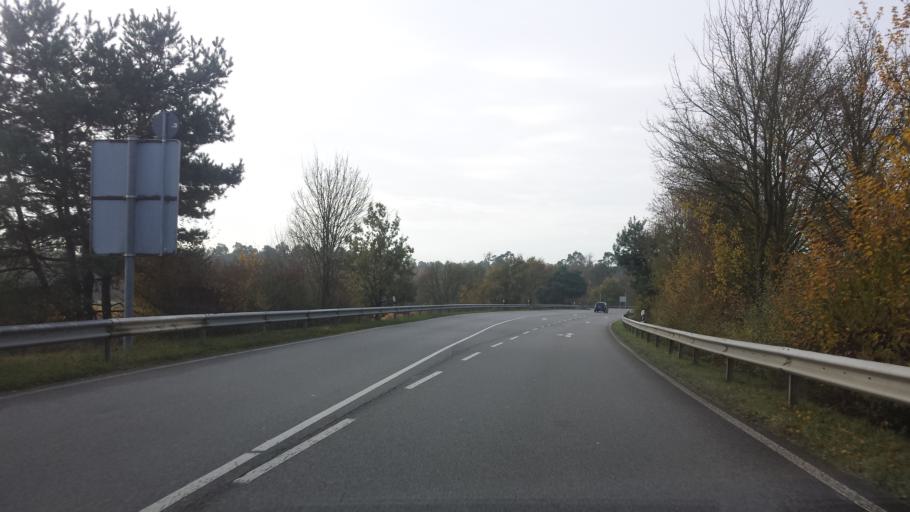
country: DE
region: Baden-Wuerttemberg
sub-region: Karlsruhe Region
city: Walldorf
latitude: 49.3228
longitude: 8.6448
